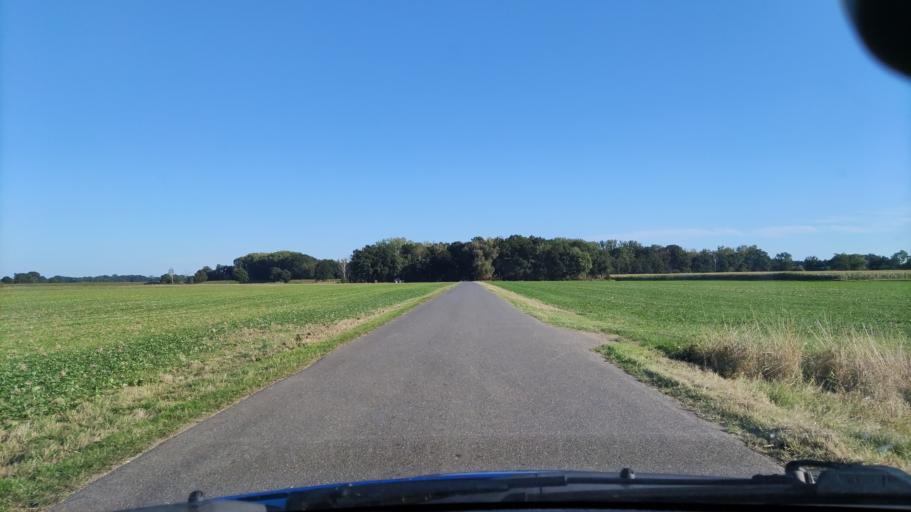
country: DE
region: Lower Saxony
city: Dannenberg
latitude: 53.1275
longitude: 11.0929
